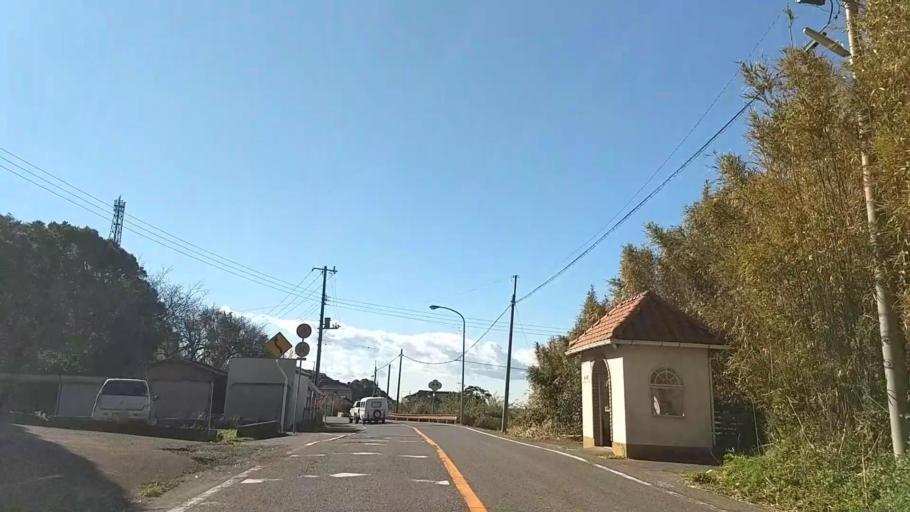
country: JP
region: Chiba
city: Tateyama
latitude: 34.9218
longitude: 139.8290
